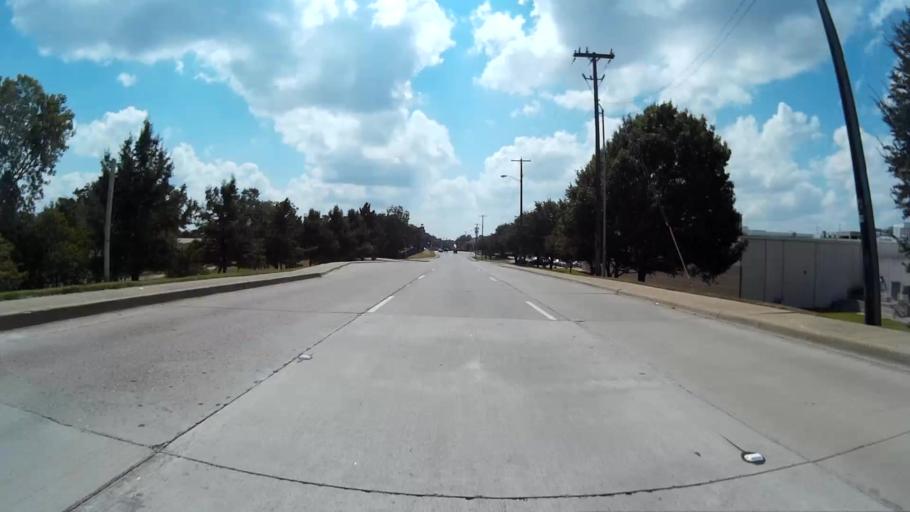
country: US
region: Texas
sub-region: Dallas County
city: Highland Park
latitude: 32.8392
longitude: -96.7701
